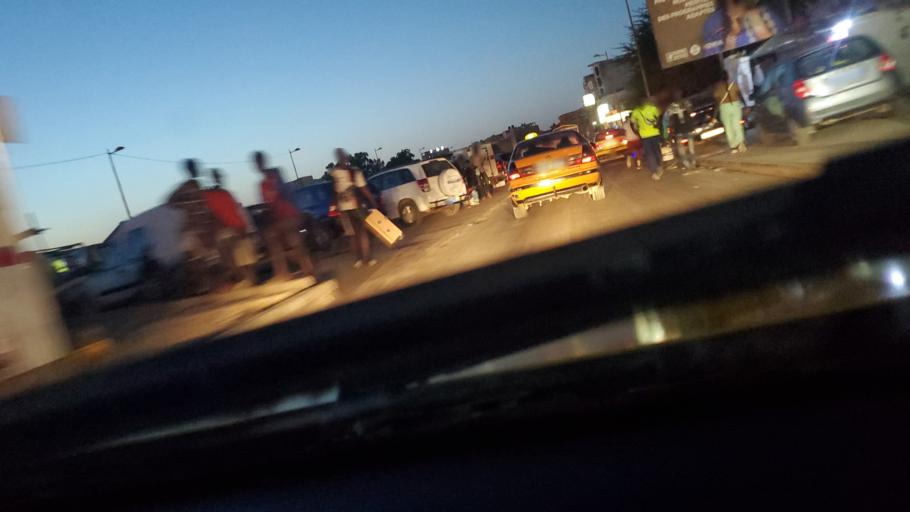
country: SN
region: Dakar
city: Dakar
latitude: 14.6780
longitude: -17.4583
